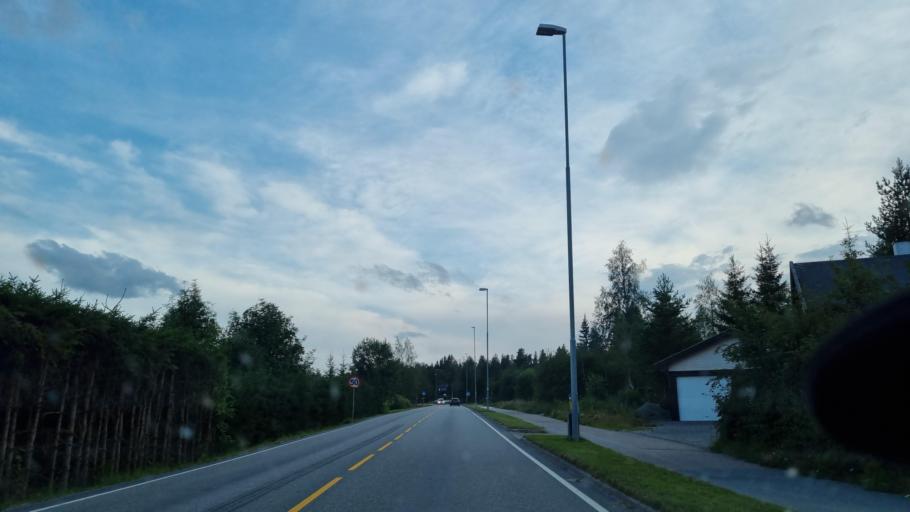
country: NO
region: Hedmark
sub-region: Trysil
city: Innbygda
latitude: 61.3092
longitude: 12.2522
